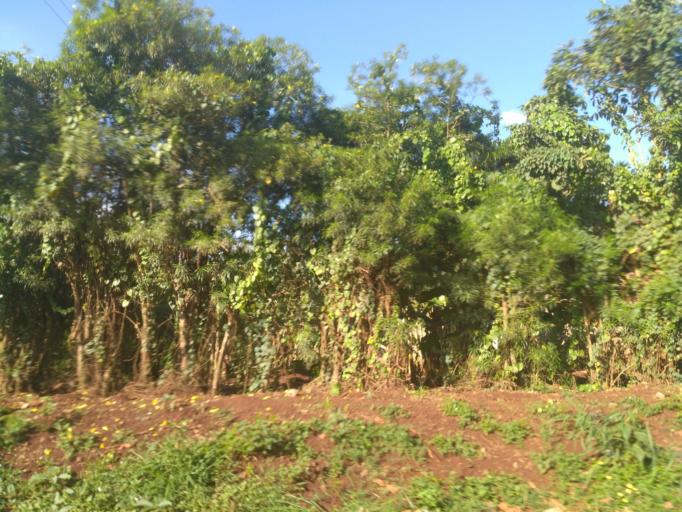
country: UG
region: Eastern Region
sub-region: Jinja District
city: Jinja
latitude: 0.4475
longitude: 33.1967
